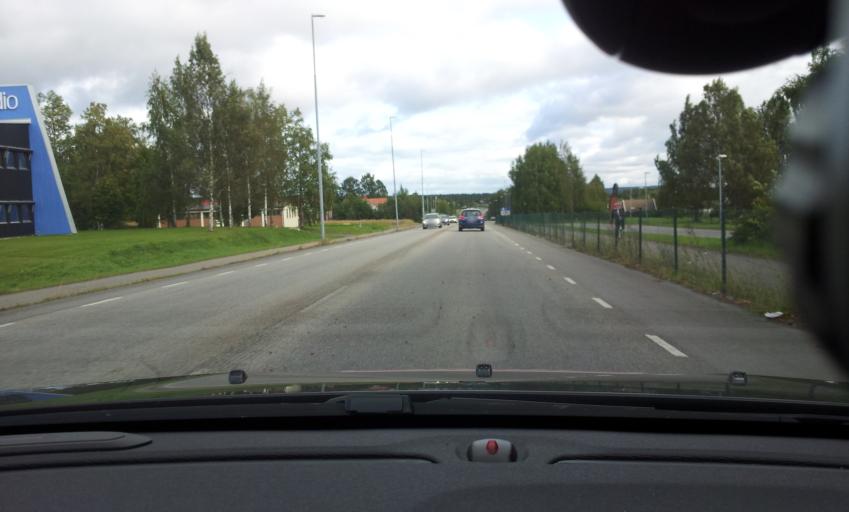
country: SE
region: Jaemtland
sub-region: OEstersunds Kommun
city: Ostersund
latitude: 63.1533
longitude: 14.6907
